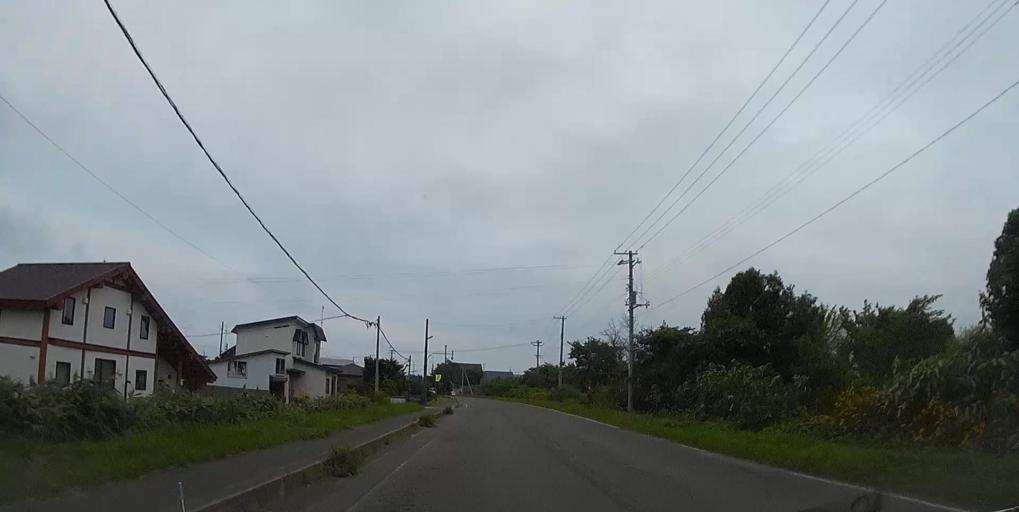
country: JP
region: Hokkaido
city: Nanae
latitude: 42.2543
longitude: 140.2549
